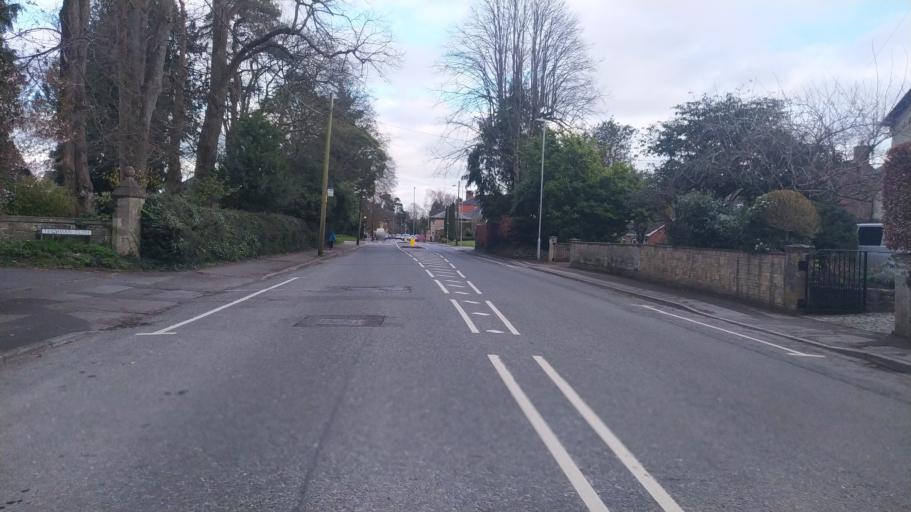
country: GB
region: England
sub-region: Wiltshire
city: Boreham
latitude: 51.2011
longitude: -2.1710
